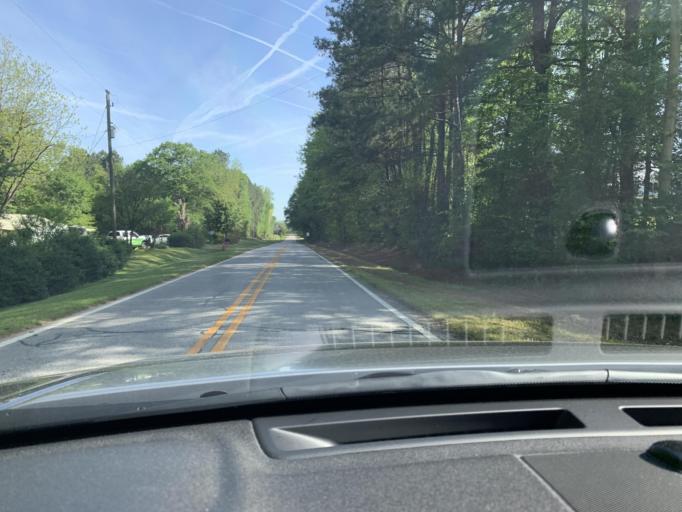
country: US
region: Georgia
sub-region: Oconee County
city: Watkinsville
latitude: 33.7957
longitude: -83.3205
